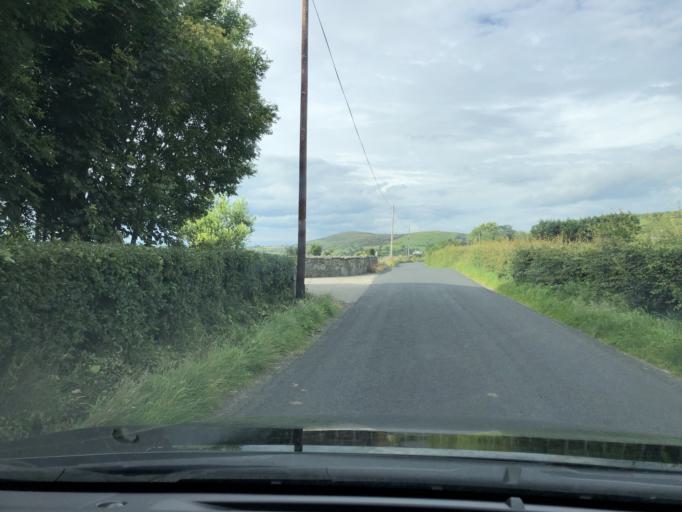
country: GB
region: Northern Ireland
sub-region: Down District
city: Castlewellan
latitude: 54.2260
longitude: -6.0139
